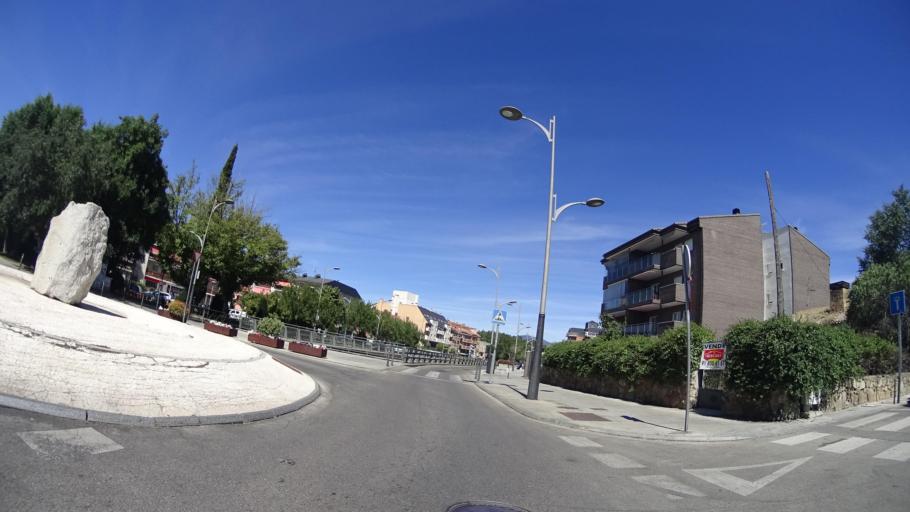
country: ES
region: Madrid
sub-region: Provincia de Madrid
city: Collado-Villalba
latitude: 40.6323
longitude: -4.0082
